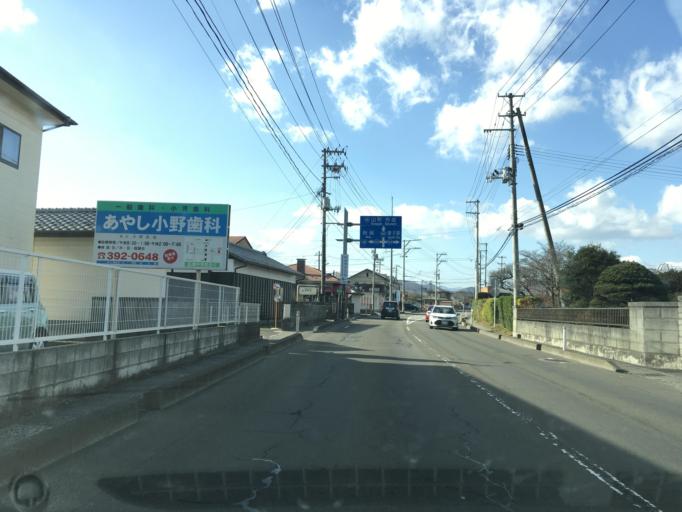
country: JP
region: Miyagi
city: Sendai
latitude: 38.2710
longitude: 140.7635
